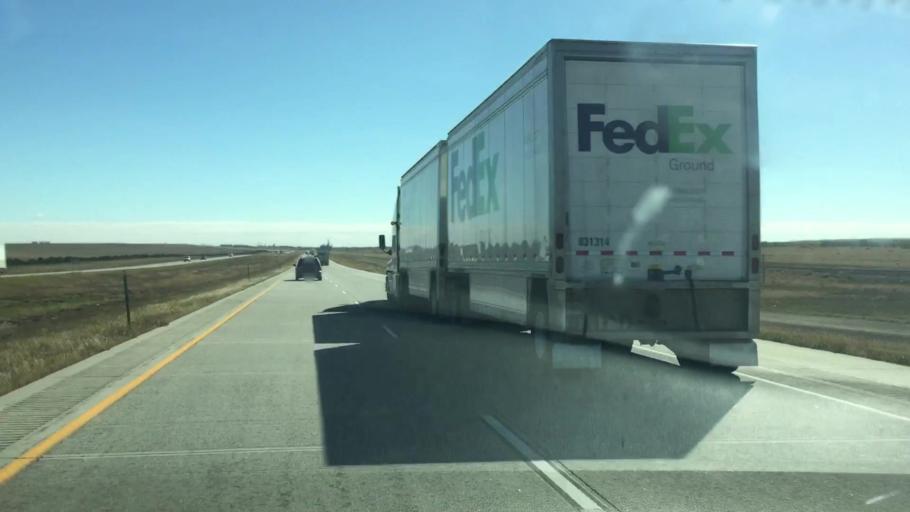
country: US
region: Colorado
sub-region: Lincoln County
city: Limon
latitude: 39.2797
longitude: -103.7645
